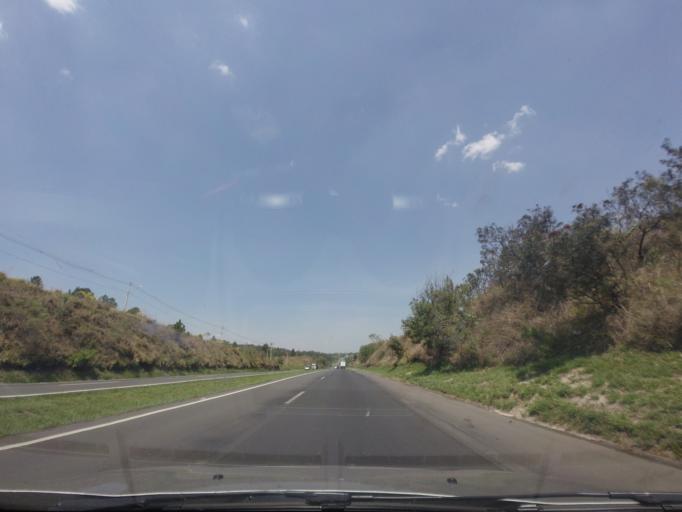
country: BR
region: Sao Paulo
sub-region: Piracicaba
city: Piracicaba
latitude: -22.7350
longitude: -47.5347
